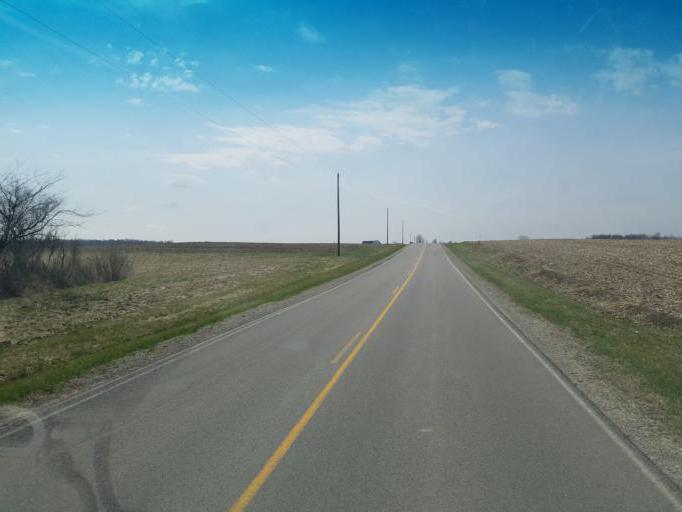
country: US
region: Ohio
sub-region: Crawford County
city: Bucyrus
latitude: 40.9108
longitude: -83.0933
